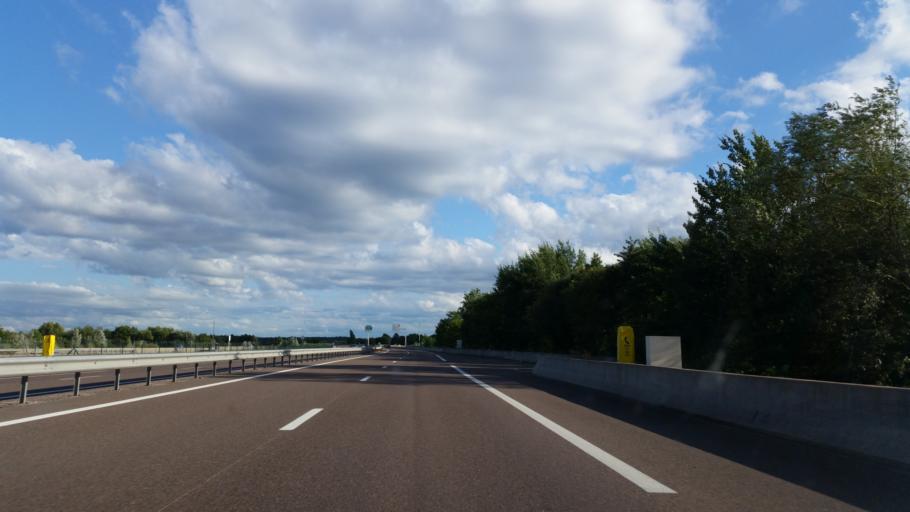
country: FR
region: Franche-Comte
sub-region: Departement de la Haute-Saone
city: Lure
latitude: 47.6815
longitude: 6.5165
